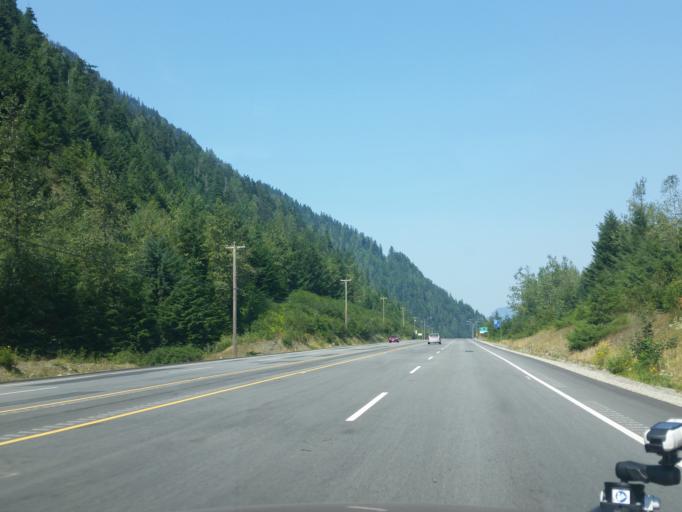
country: CA
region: British Columbia
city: Hope
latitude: 49.2949
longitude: -121.2608
